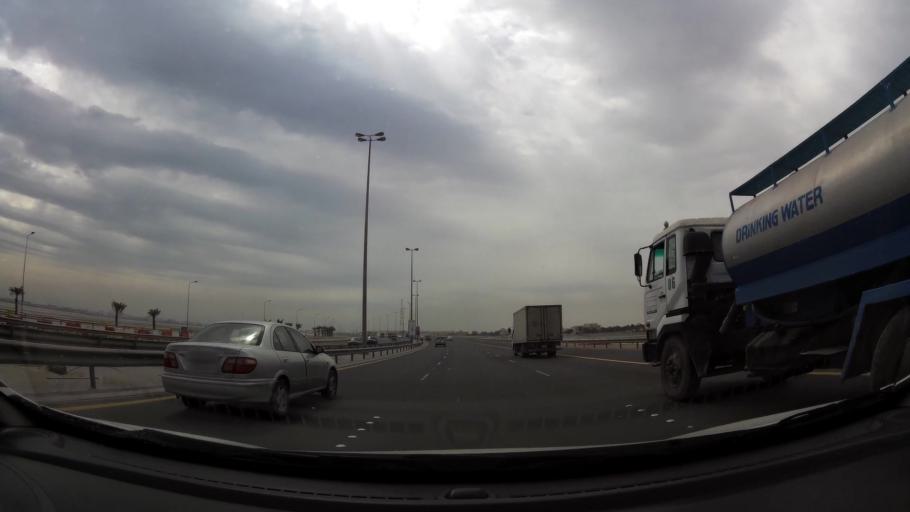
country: BH
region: Manama
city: Manama
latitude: 26.1915
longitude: 50.5885
